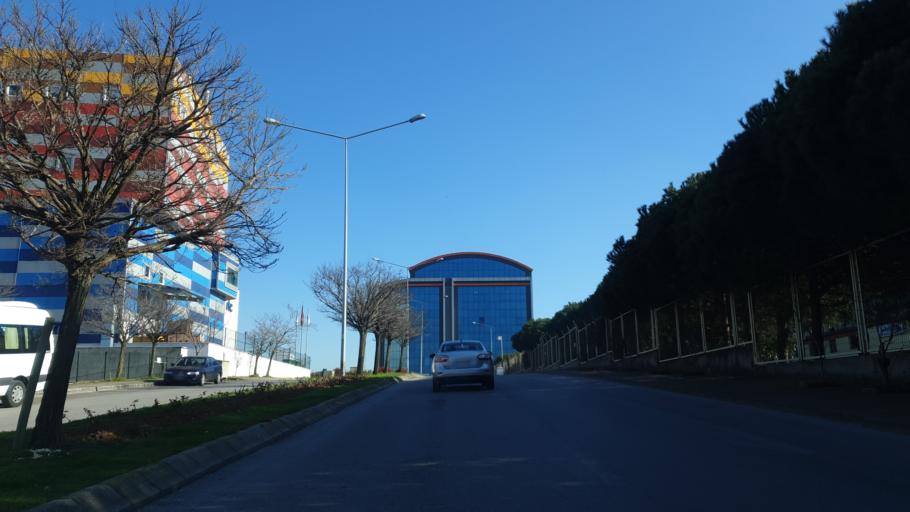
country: TR
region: Kocaeli
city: Balcik
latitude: 40.8765
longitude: 29.3722
